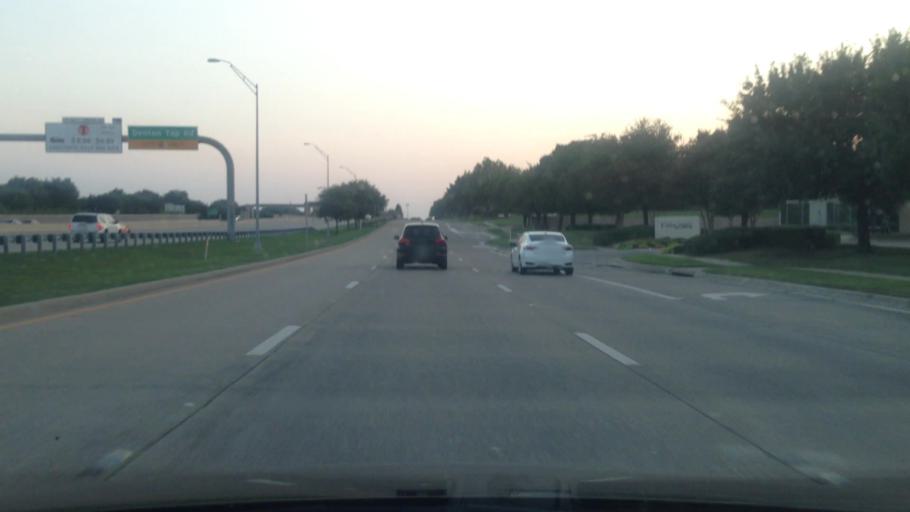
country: US
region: Texas
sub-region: Dallas County
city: Coppell
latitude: 32.9904
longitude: -96.9801
